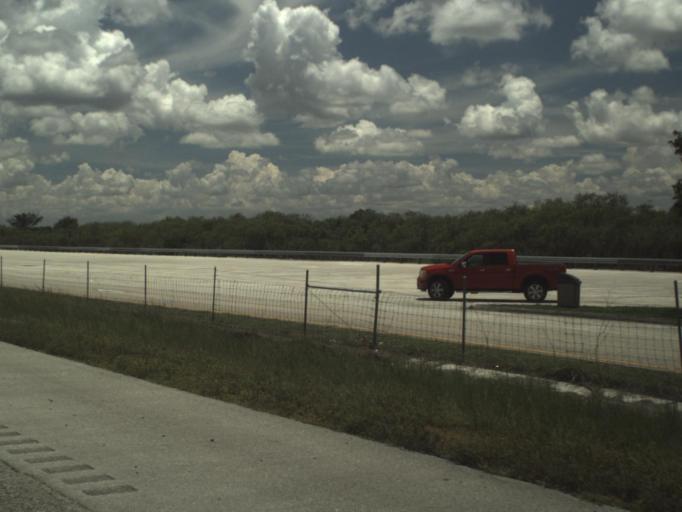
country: US
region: Florida
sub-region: Broward County
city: Weston
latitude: 26.1490
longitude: -80.7172
